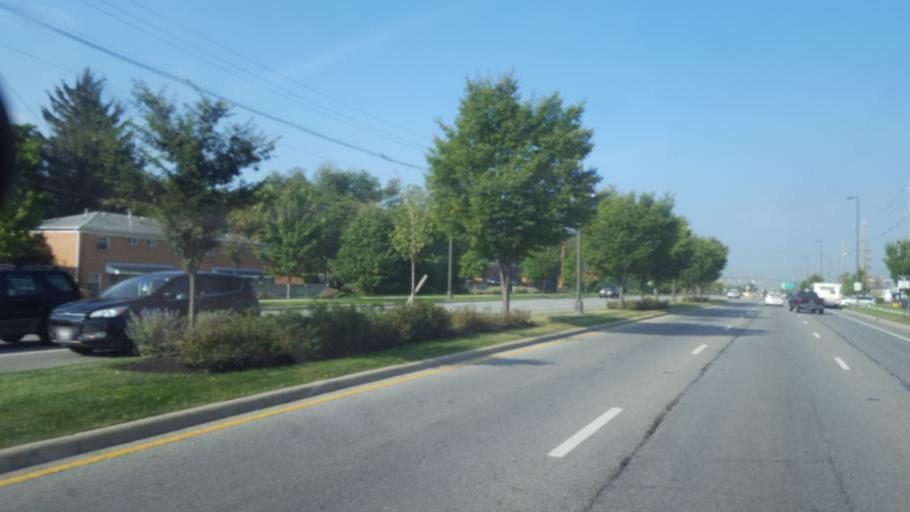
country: US
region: Ohio
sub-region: Franklin County
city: Worthington
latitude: 40.0615
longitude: -82.9889
